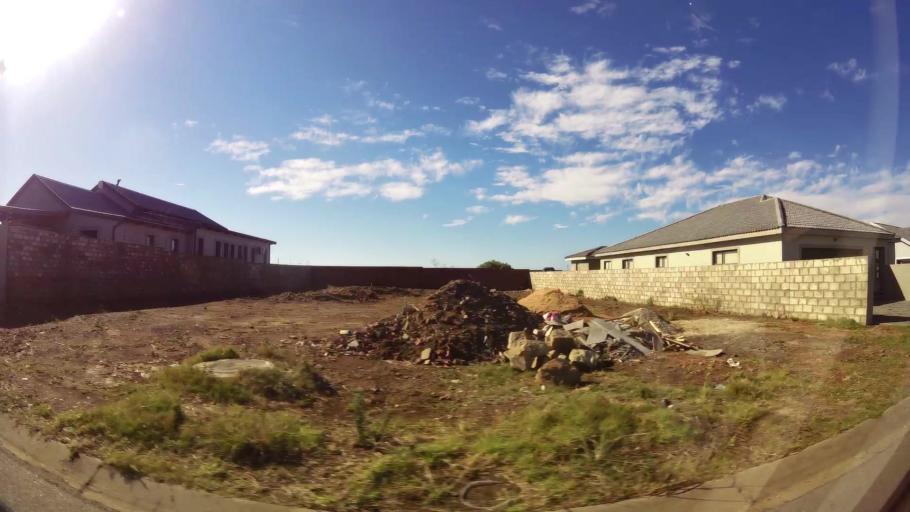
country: ZA
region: Eastern Cape
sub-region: Cacadu District Municipality
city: Jeffrey's Bay
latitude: -34.0382
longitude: 24.9081
